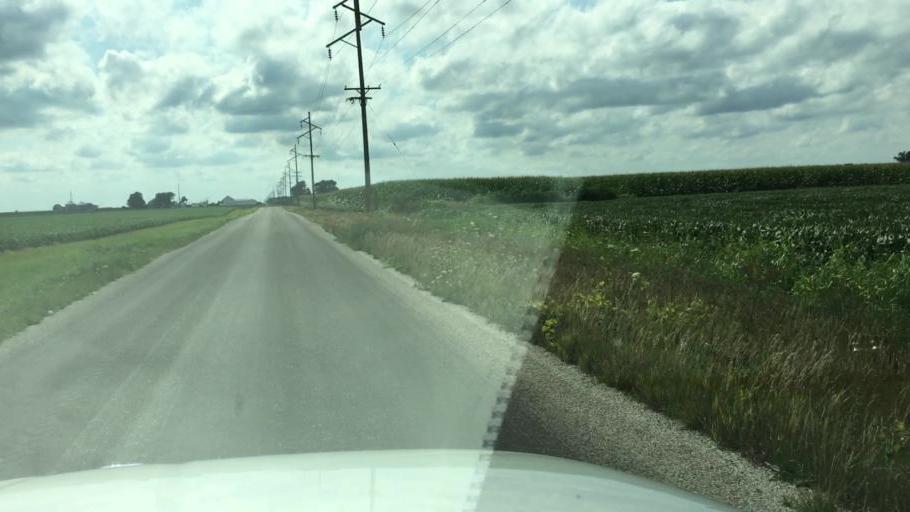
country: US
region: Illinois
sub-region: Hancock County
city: Carthage
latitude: 40.4168
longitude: -91.1683
